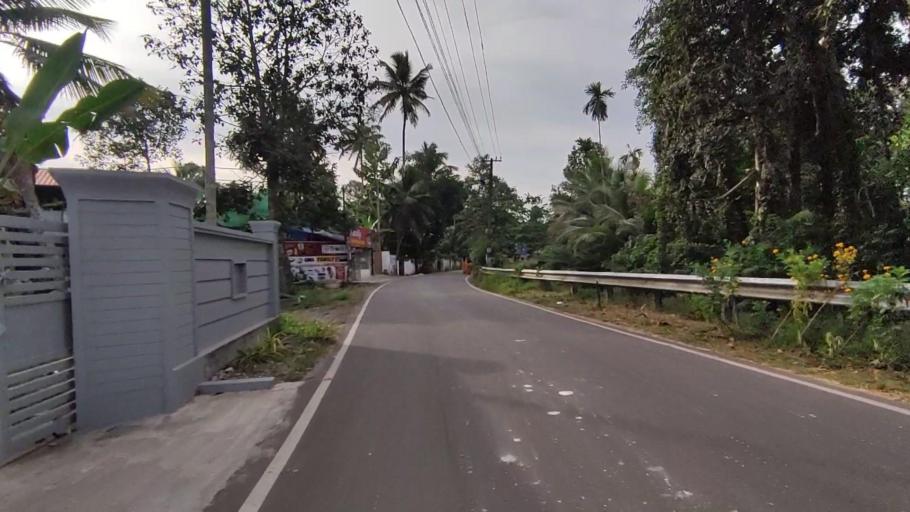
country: IN
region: Kerala
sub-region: Kottayam
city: Kottayam
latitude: 9.6029
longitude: 76.4918
